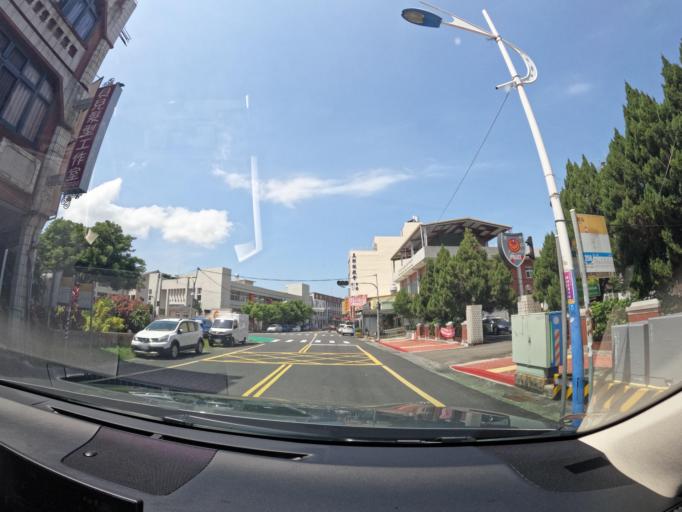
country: TW
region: Taiwan
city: Fengyuan
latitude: 24.3124
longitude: 120.8256
